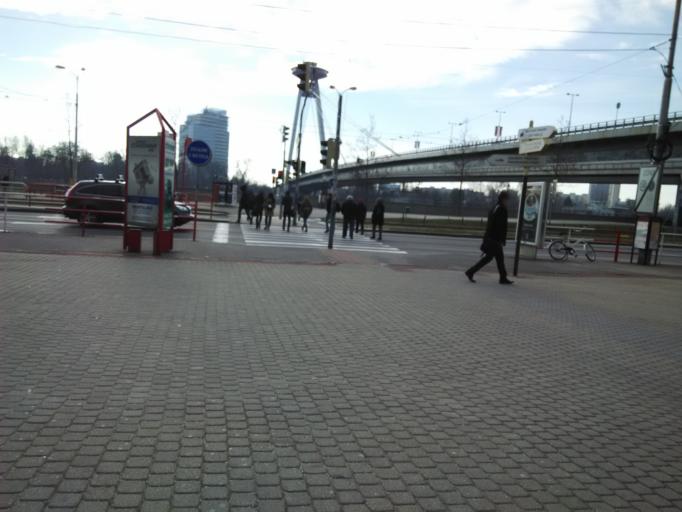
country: SK
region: Bratislavsky
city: Bratislava
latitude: 48.1401
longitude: 17.1053
